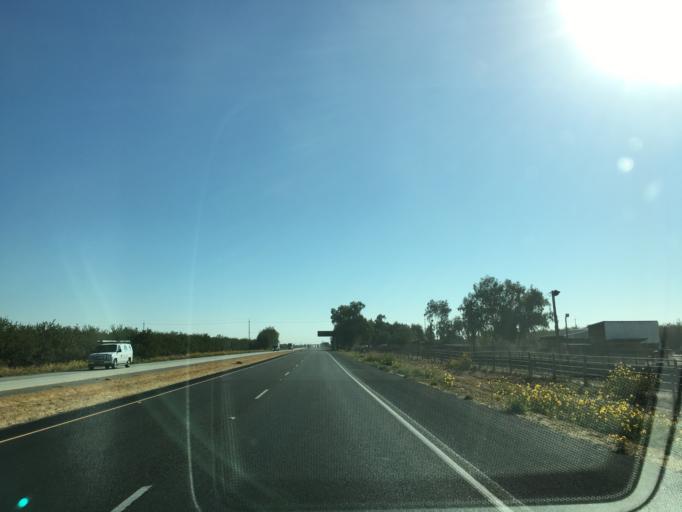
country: US
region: California
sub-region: Madera County
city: Chowchilla
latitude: 37.0834
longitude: -120.3157
